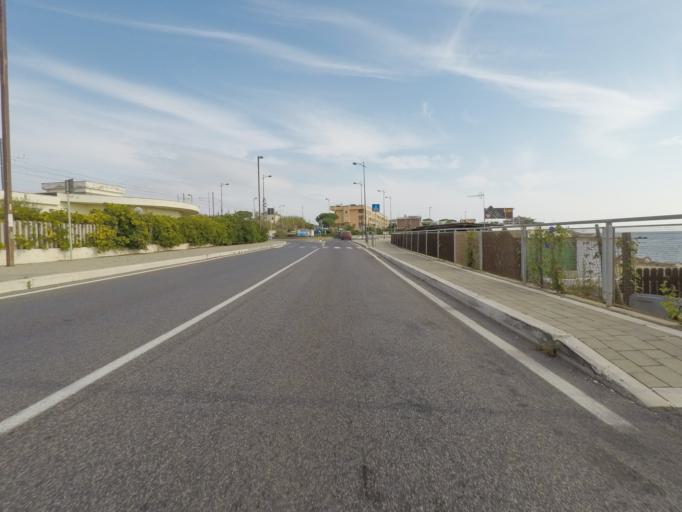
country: IT
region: Latium
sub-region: Citta metropolitana di Roma Capitale
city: Santa Marinella
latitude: 42.0449
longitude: 11.8262
